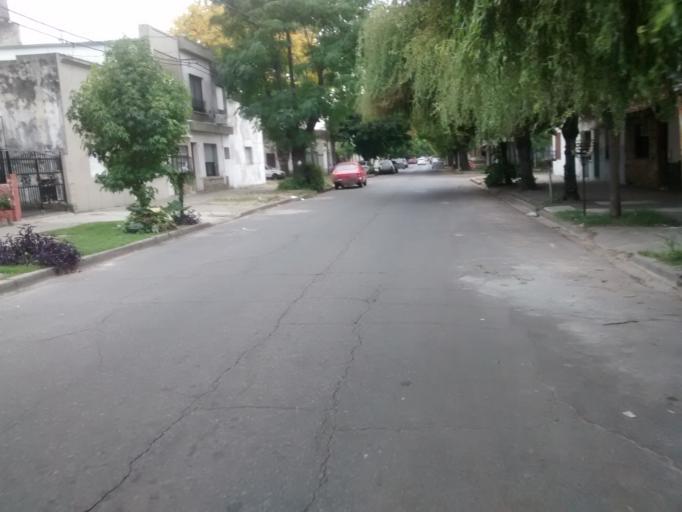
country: AR
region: Buenos Aires
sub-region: Partido de La Plata
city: La Plata
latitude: -34.9374
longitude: -57.9409
